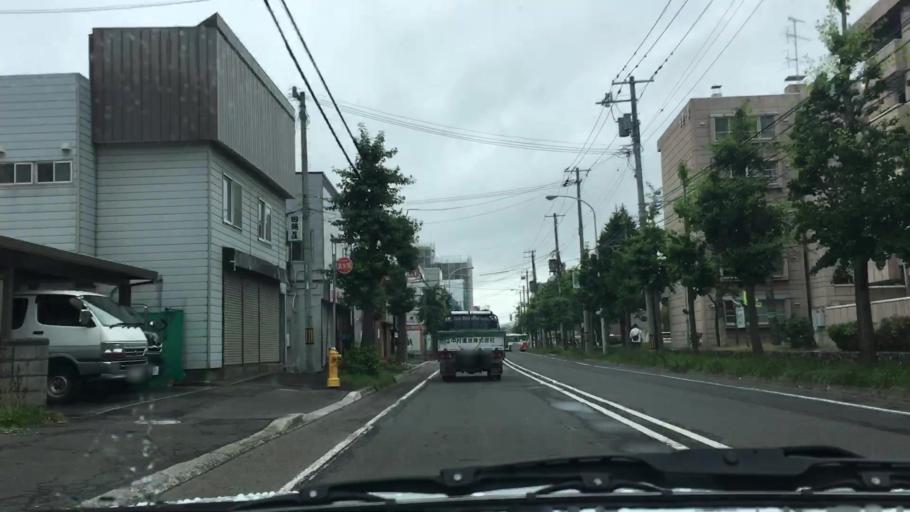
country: JP
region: Hokkaido
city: Sapporo
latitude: 43.0764
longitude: 141.3850
